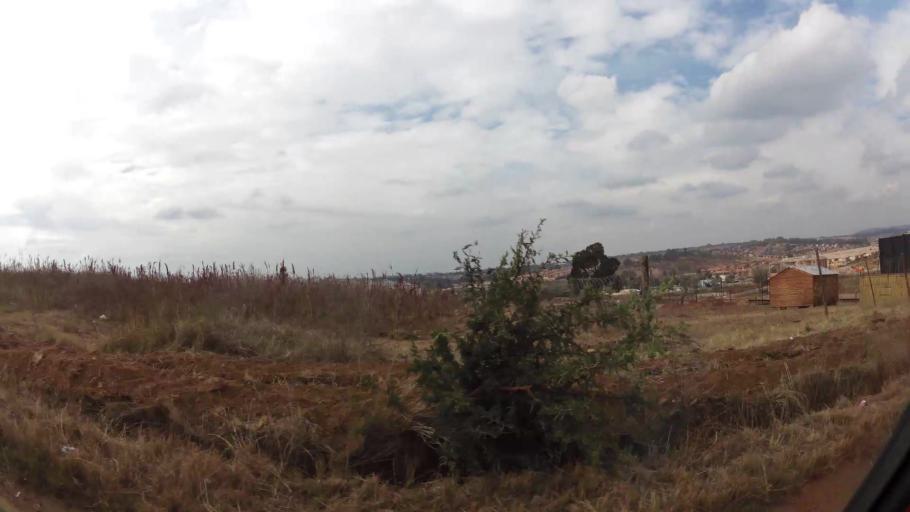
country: ZA
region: Gauteng
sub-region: City of Johannesburg Metropolitan Municipality
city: Roodepoort
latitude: -26.1045
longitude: 27.8817
